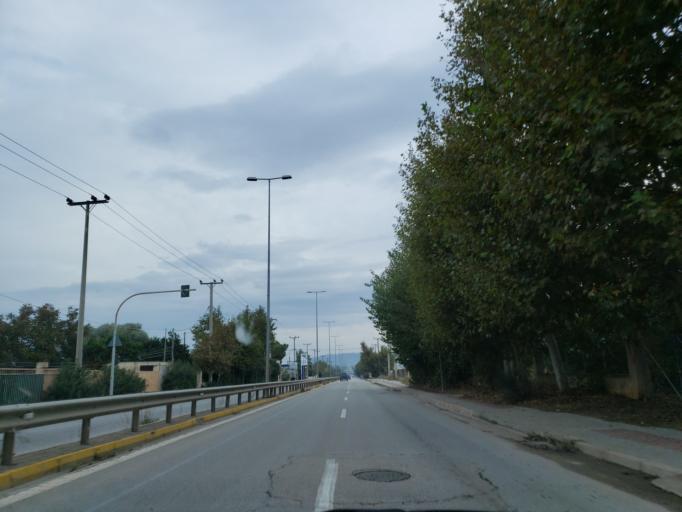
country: GR
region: Attica
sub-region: Nomarchia Anatolikis Attikis
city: Aghios Panteleimon
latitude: 38.1148
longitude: 23.9698
